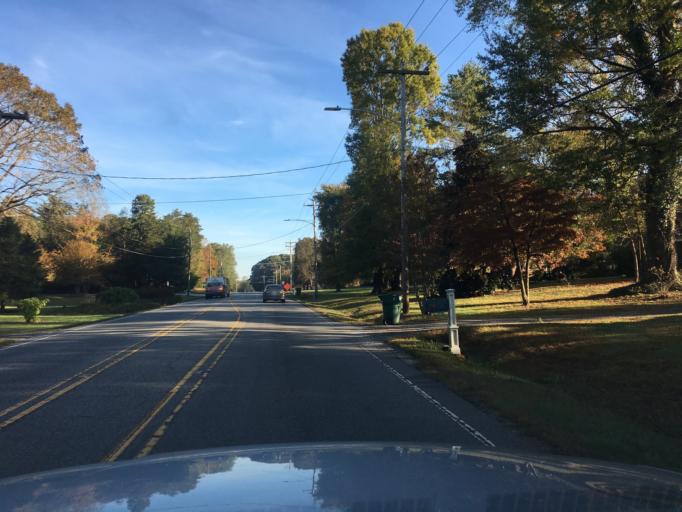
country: US
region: North Carolina
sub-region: Catawba County
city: Newton
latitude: 35.6494
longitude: -81.2678
